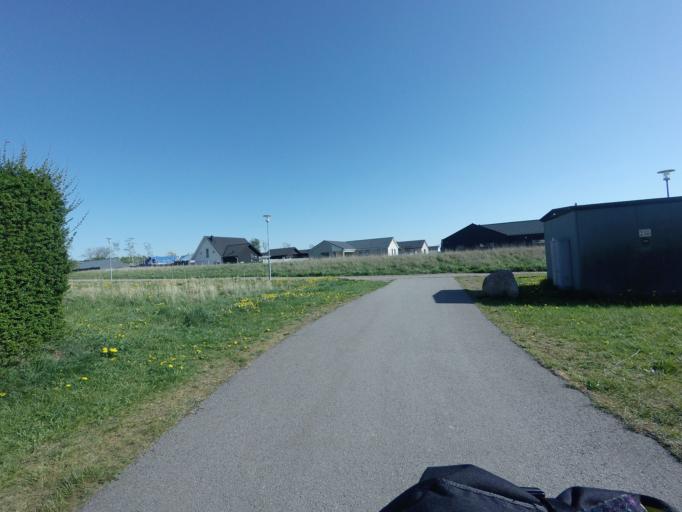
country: SE
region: Skane
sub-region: Landskrona
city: Asmundtorp
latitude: 55.8520
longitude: 12.9085
